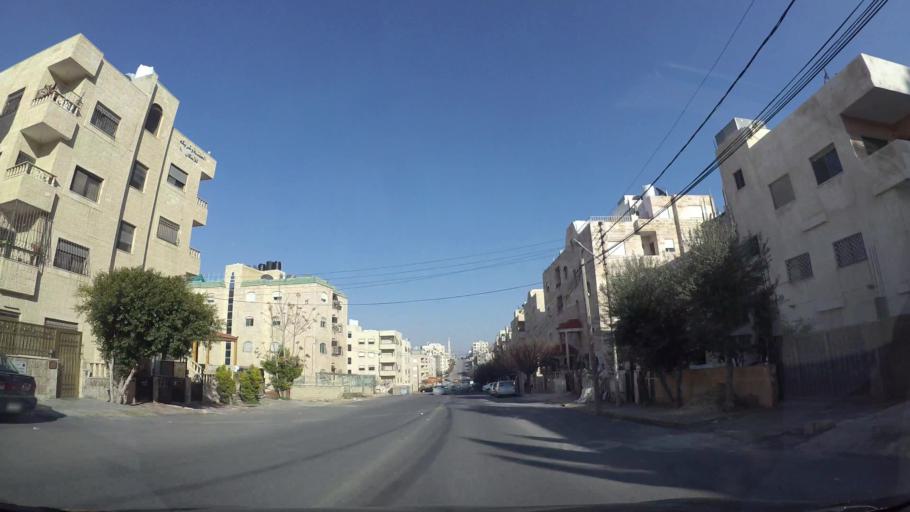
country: JO
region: Amman
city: Amman
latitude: 31.9803
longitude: 35.9509
